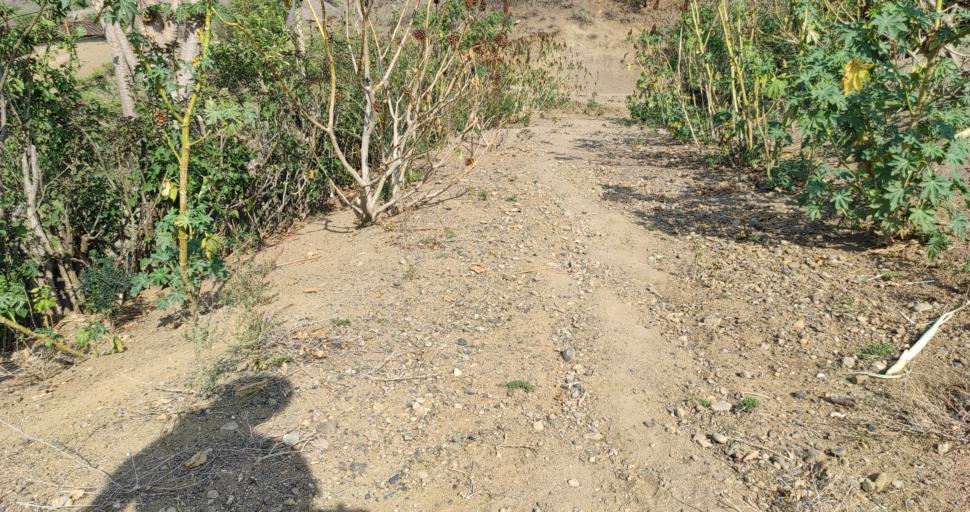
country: EC
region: Loja
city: Catacocha
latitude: -4.0047
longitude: -79.7159
